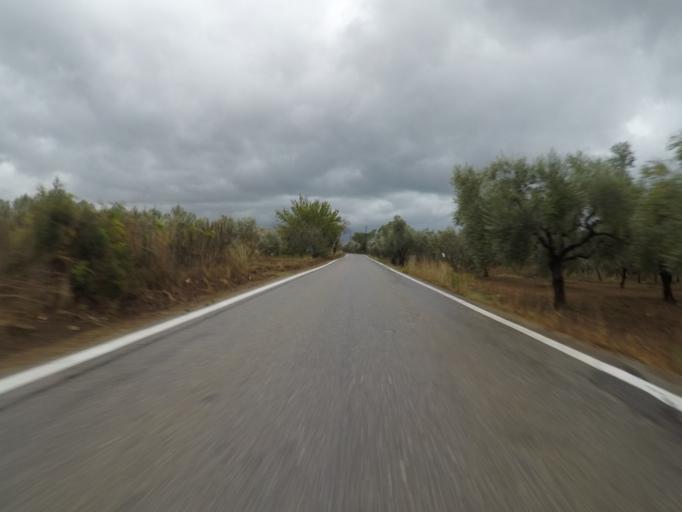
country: GR
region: Peloponnese
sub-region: Nomos Messinias
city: Pylos
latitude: 36.9825
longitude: 21.6846
